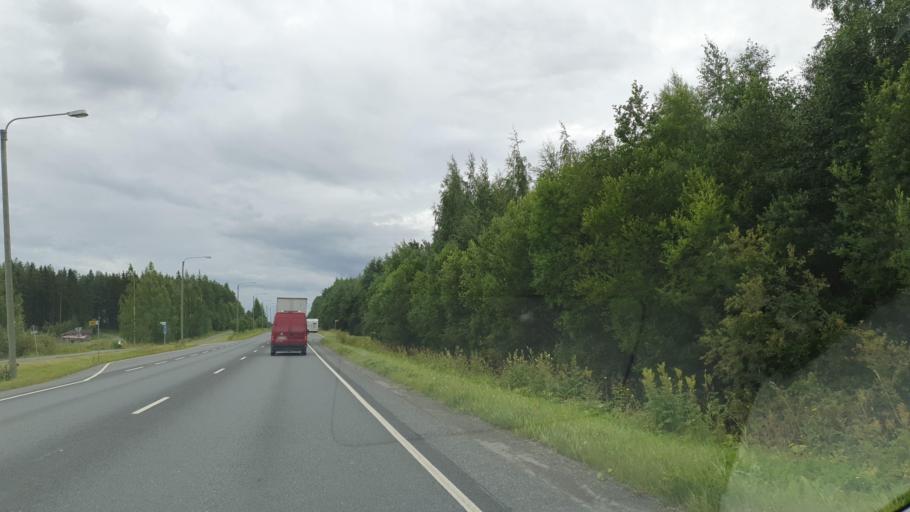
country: FI
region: Northern Savo
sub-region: Ylae-Savo
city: Lapinlahti
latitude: 63.4509
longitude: 27.3189
